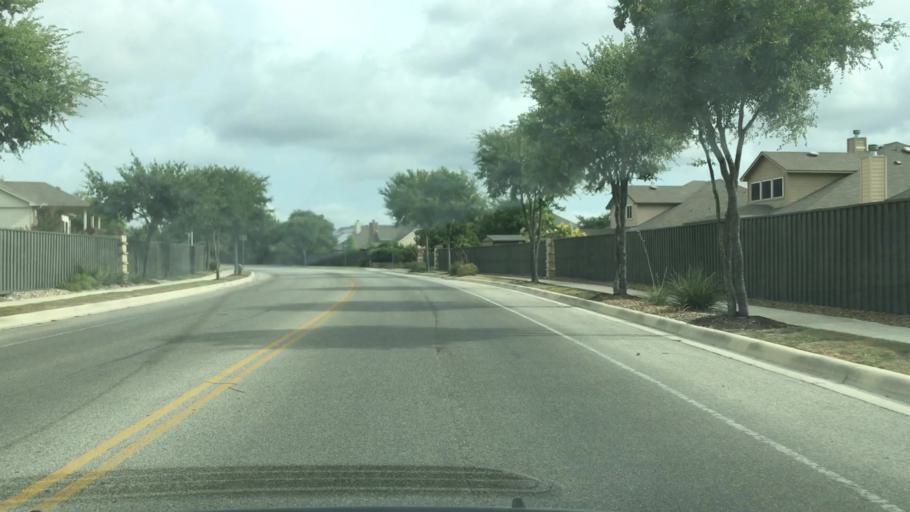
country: US
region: Texas
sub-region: Guadalupe County
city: Cibolo
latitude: 29.5797
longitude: -98.2397
